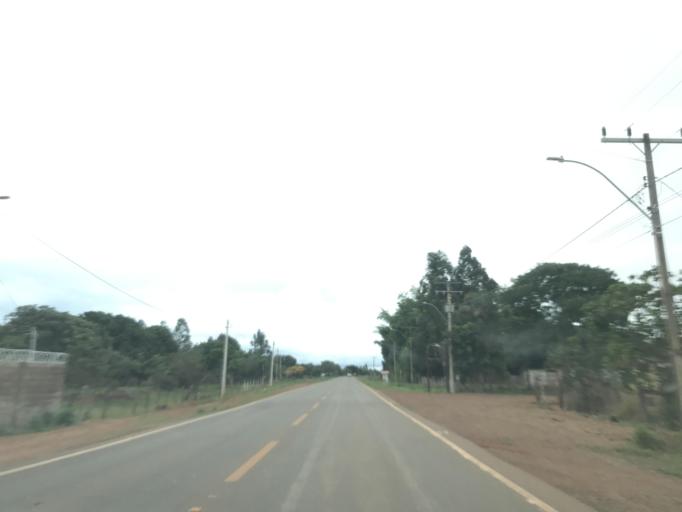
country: BR
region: Goias
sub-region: Luziania
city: Luziania
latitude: -16.3306
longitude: -48.0192
